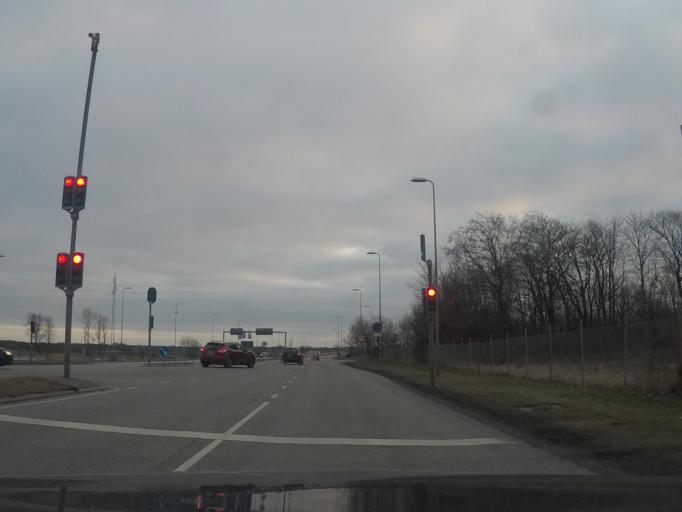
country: DK
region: Central Jutland
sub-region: Herning Kommune
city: Herning
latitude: 56.1168
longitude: 8.9463
